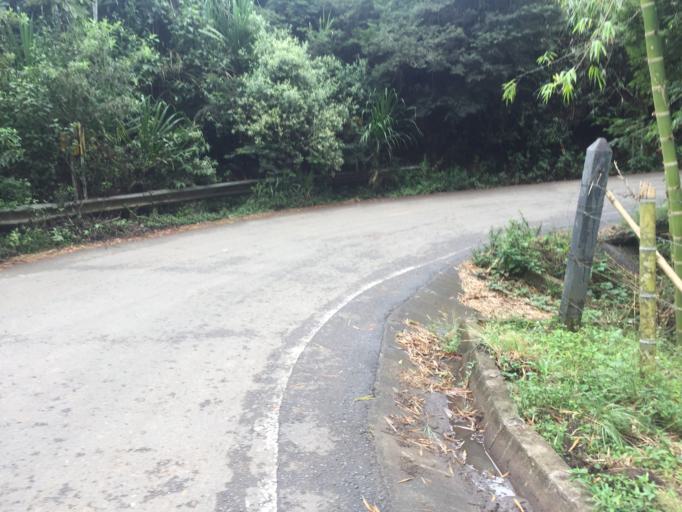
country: CO
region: Valle del Cauca
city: Dagua
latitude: 3.6887
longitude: -76.5936
